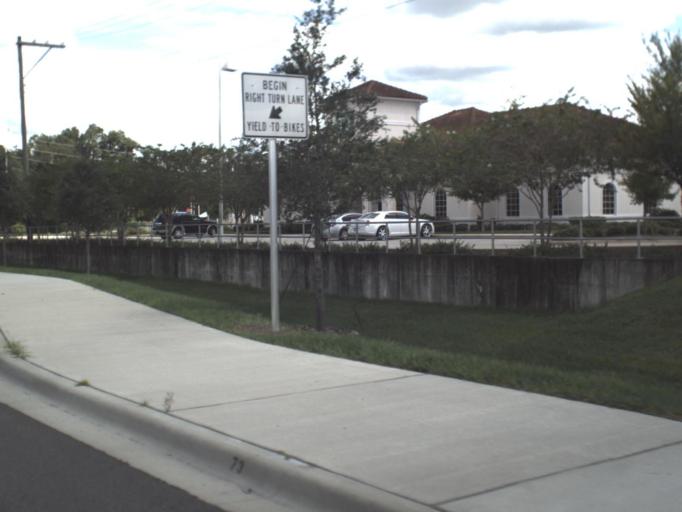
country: US
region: Florida
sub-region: Polk County
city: Bartow
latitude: 27.9039
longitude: -81.8382
